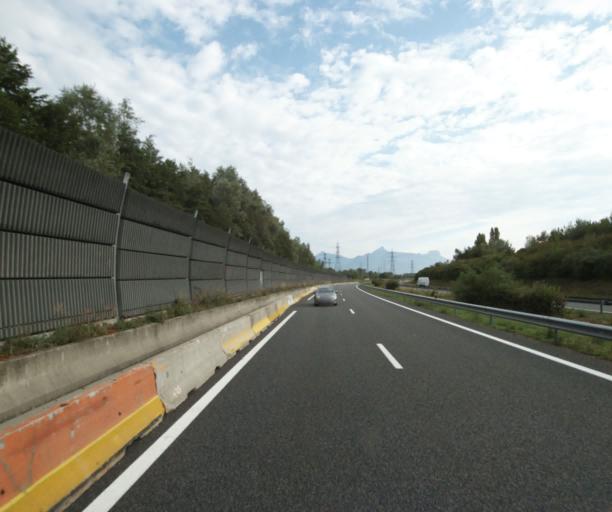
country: FR
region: Rhone-Alpes
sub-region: Departement de l'Isere
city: Allieres-et-Risset
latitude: 45.0938
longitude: 5.6700
